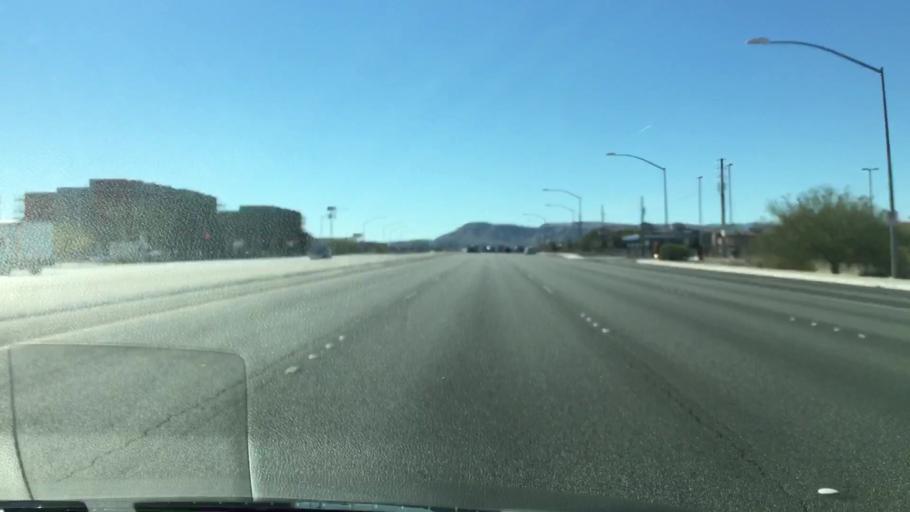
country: US
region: Nevada
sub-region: Clark County
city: Whitney
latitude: 35.9953
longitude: -115.1309
